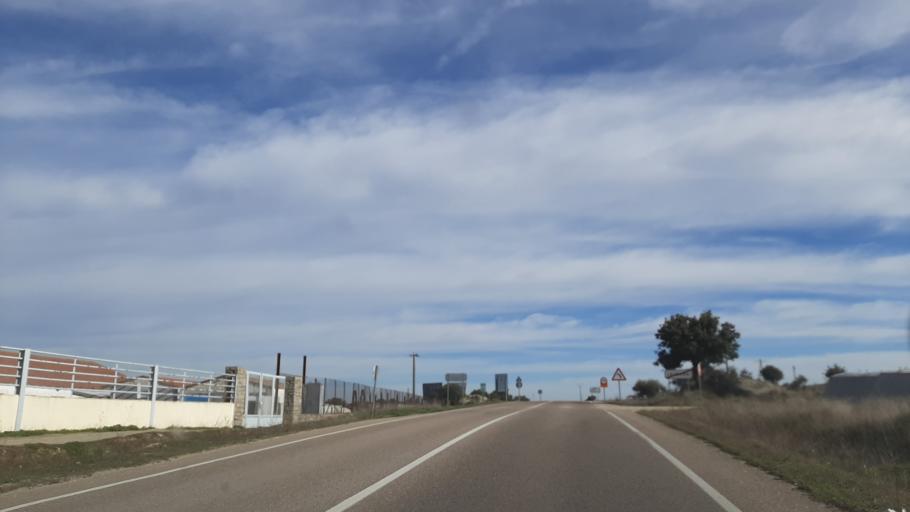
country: ES
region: Castille and Leon
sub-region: Provincia de Salamanca
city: Ledesma
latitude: 41.0917
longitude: -5.9911
